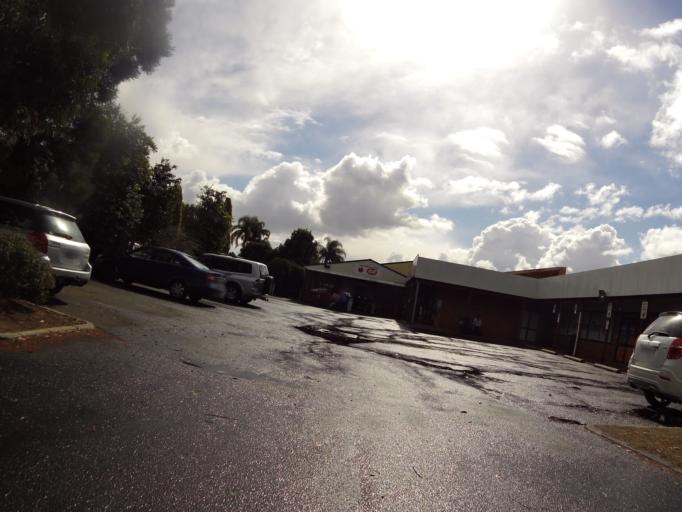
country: AU
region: Western Australia
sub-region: Donnybrook-Balingup
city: Donnybrook
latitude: -33.5704
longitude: 115.8240
